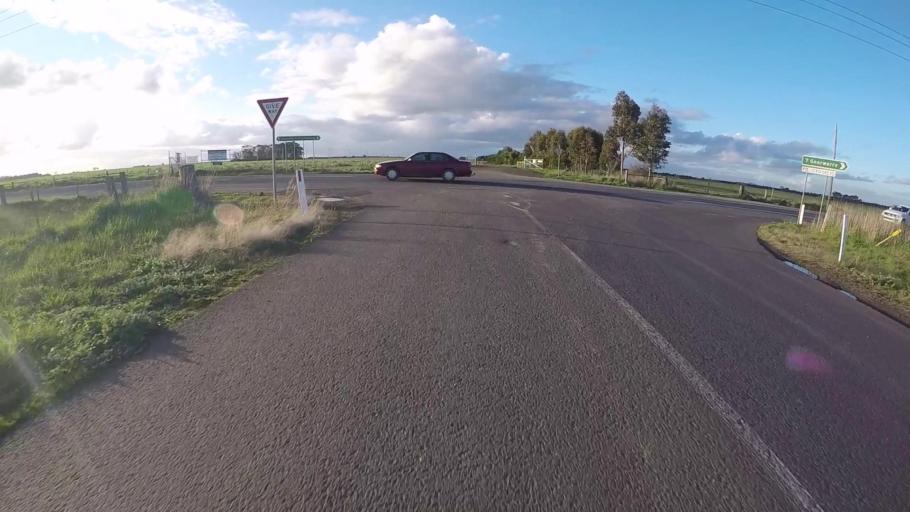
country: AU
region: Victoria
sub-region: Greater Geelong
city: Wandana Heights
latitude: -38.1220
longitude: 144.2067
